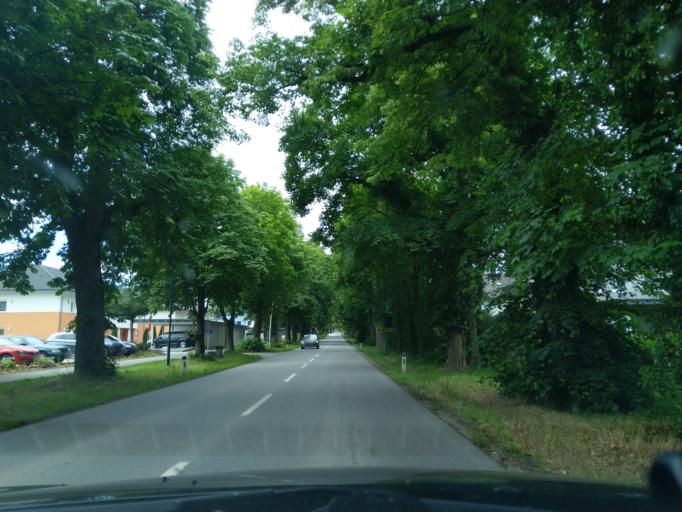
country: AT
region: Upper Austria
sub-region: Politischer Bezirk Scharding
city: Sankt Marienkirchen bei Schaerding
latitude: 48.2929
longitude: 13.4368
